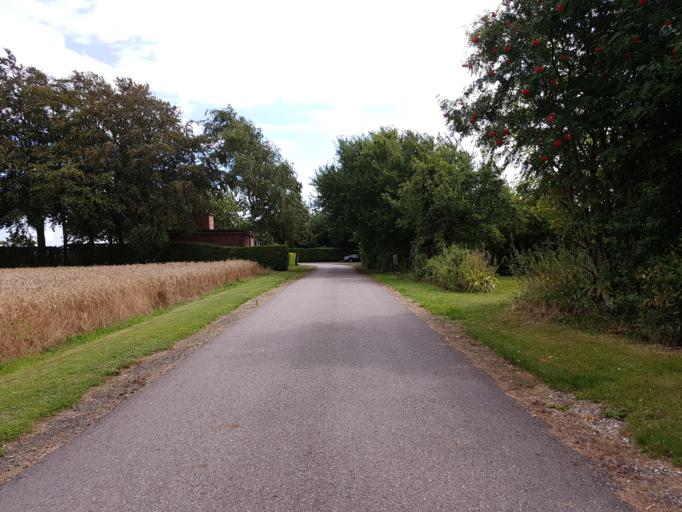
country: DK
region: Zealand
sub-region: Guldborgsund Kommune
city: Nykobing Falster
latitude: 54.5803
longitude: 11.9405
